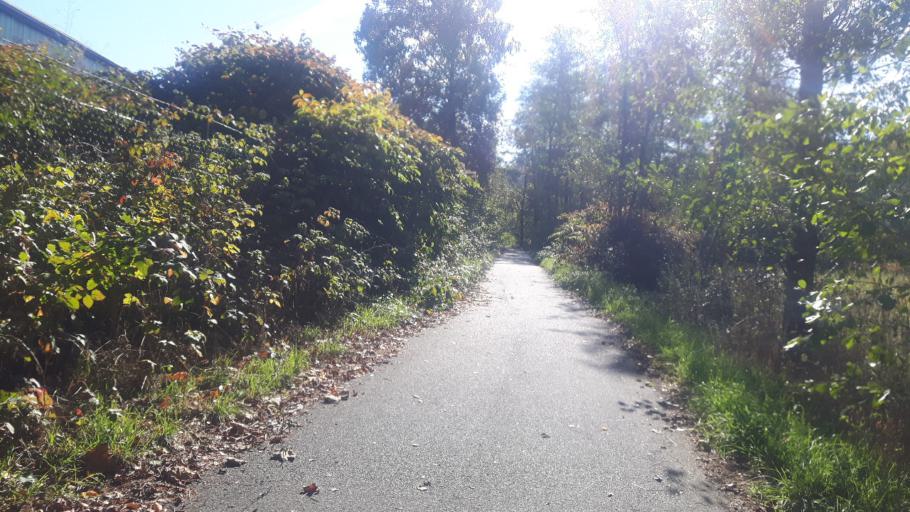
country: DE
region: Rheinland-Pfalz
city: Niederirsen
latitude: 50.7973
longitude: 7.6053
